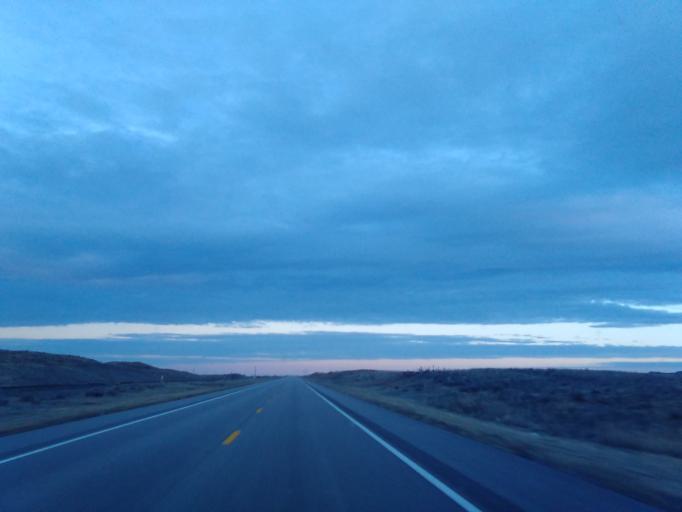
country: US
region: Nebraska
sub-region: Garden County
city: Oshkosh
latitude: 41.3770
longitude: -102.2610
